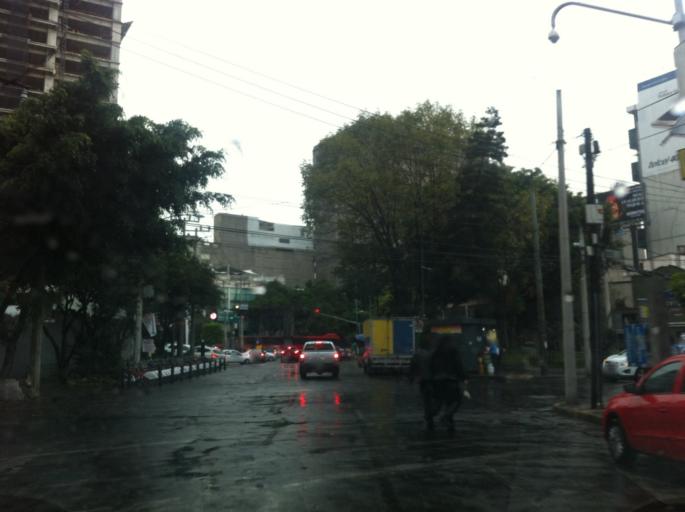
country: MX
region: Mexico City
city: Colonia del Valle
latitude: 19.3695
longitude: -99.1793
